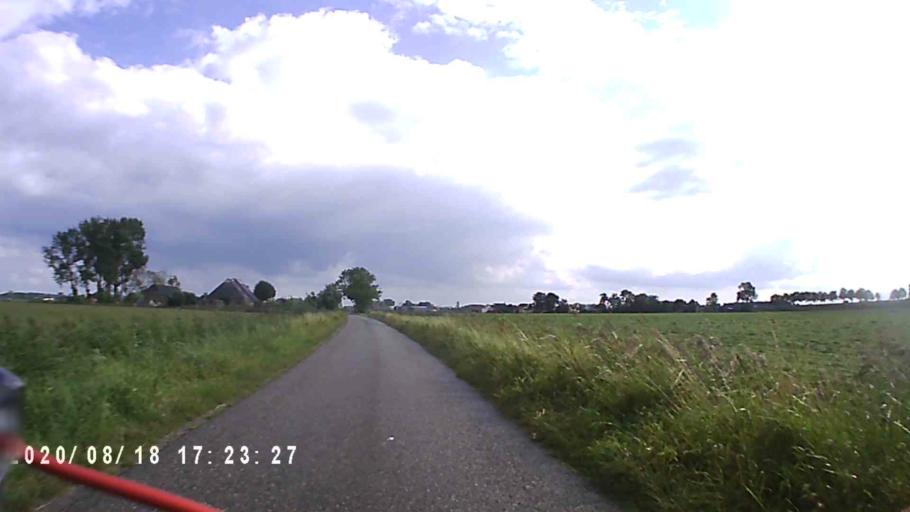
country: NL
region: Groningen
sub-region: Gemeente Zuidhorn
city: Aduard
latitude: 53.2481
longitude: 6.4884
